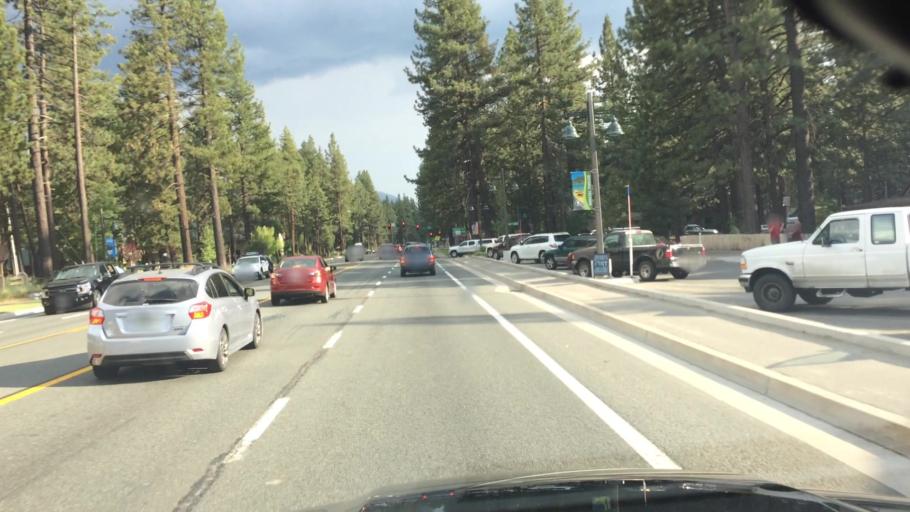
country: US
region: California
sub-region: El Dorado County
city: South Lake Tahoe
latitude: 38.9398
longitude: -119.9773
